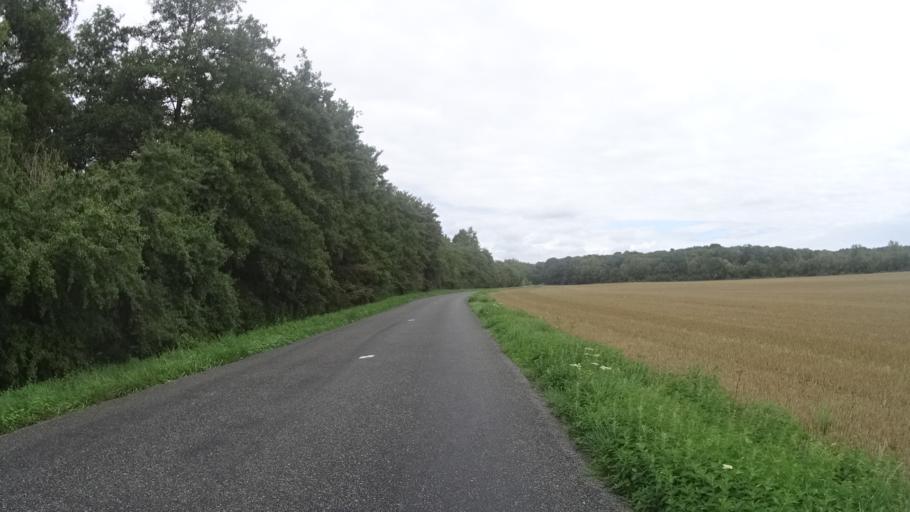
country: FR
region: Picardie
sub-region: Departement de l'Oise
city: Chiry-Ourscamp
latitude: 49.5375
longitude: 2.9737
